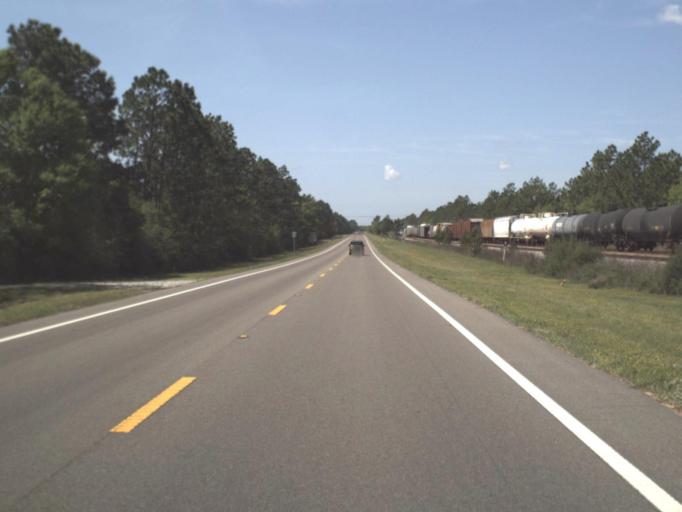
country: US
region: Florida
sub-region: Santa Rosa County
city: East Milton
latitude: 30.6713
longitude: -86.8625
